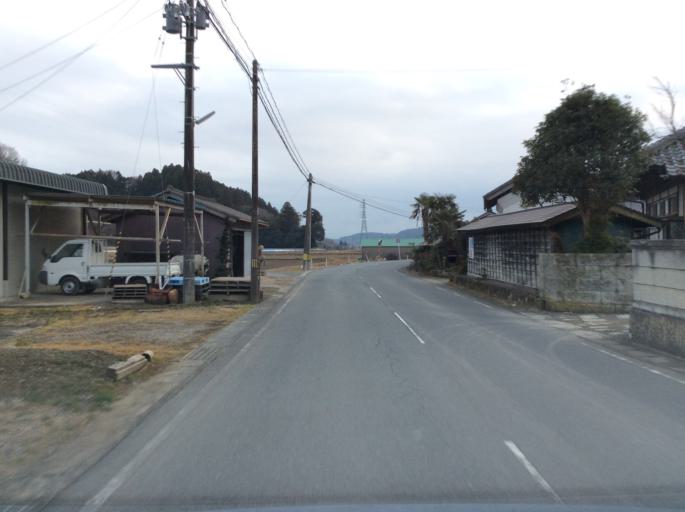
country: JP
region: Fukushima
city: Iwaki
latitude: 37.1273
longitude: 140.9533
